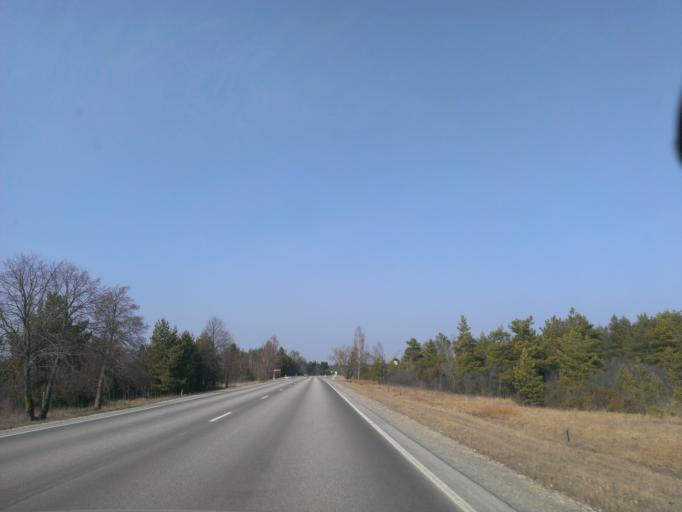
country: EE
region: Saare
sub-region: Orissaare vald
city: Orissaare
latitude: 58.5791
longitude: 23.1653
